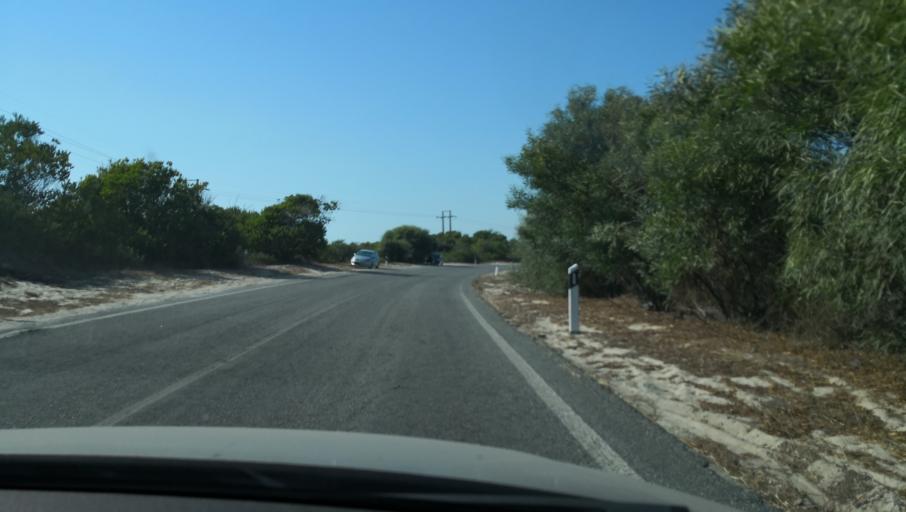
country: PT
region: Setubal
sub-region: Setubal
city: Setubal
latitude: 38.4191
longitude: -8.8192
